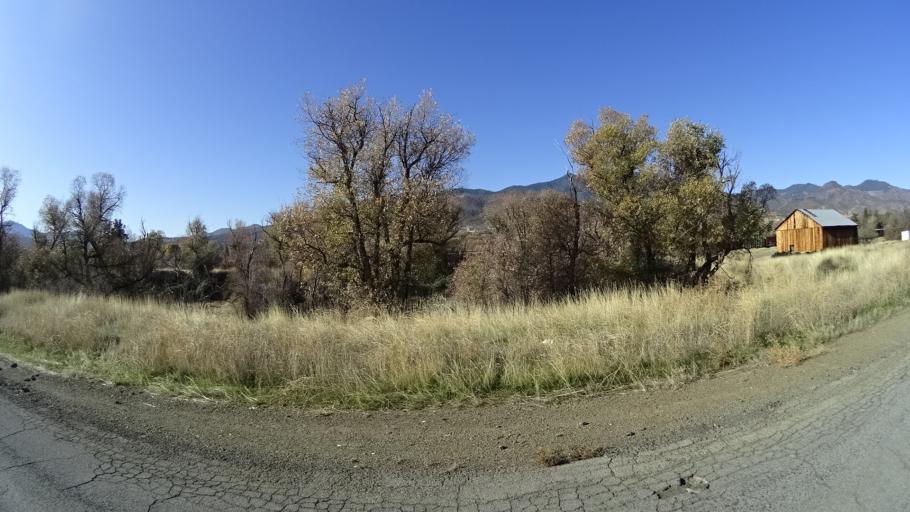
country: US
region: California
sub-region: Siskiyou County
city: Montague
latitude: 41.9070
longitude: -122.5503
